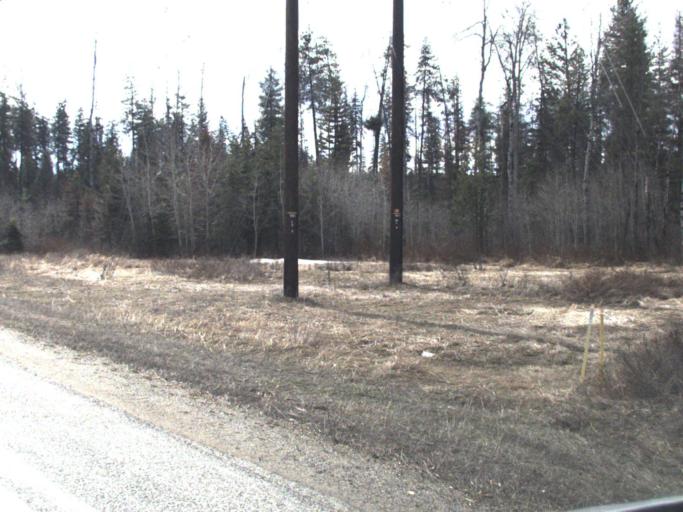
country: US
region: Washington
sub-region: Pend Oreille County
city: Newport
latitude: 48.2890
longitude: -117.2731
